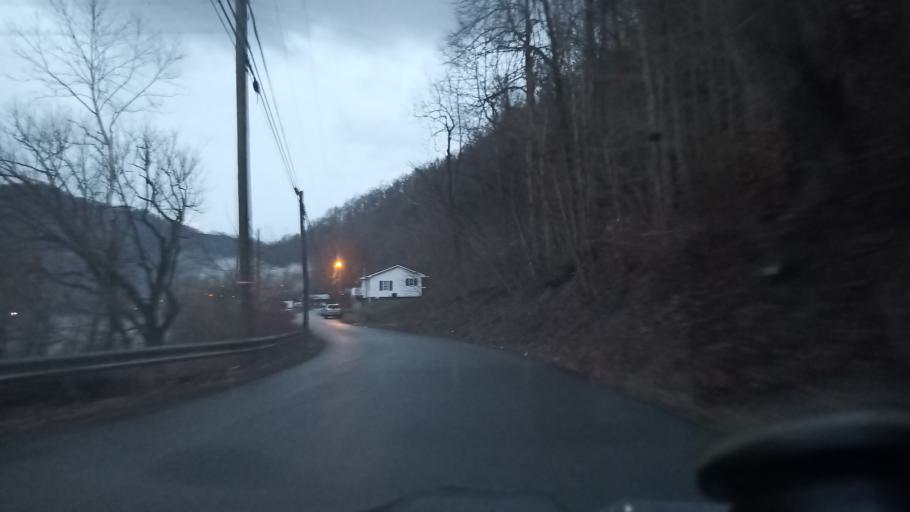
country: US
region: West Virginia
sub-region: Logan County
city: Mallory
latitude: 37.7270
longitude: -81.8774
